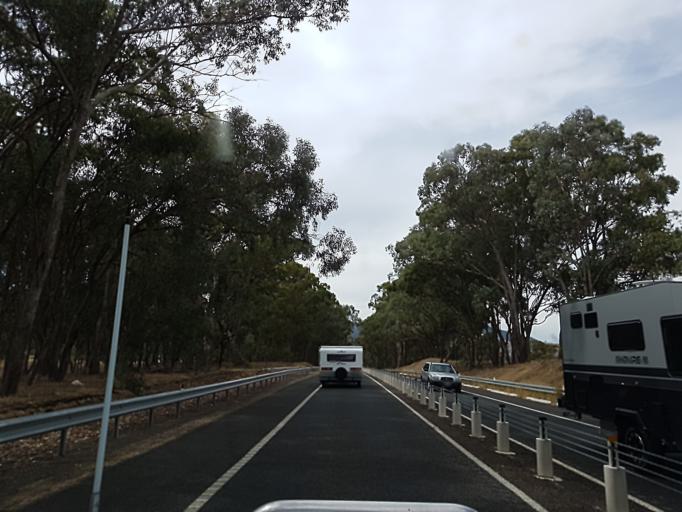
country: AU
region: Victoria
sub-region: Murrindindi
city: Alexandra
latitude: -37.1761
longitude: 145.4983
